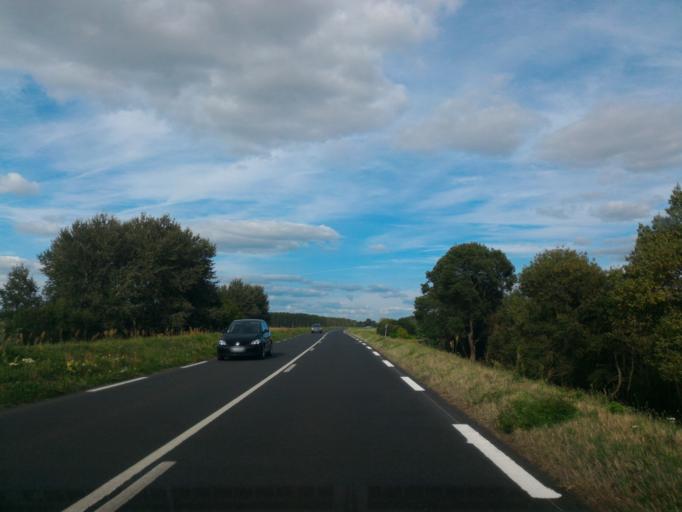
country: FR
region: Centre
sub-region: Departement du Loir-et-Cher
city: Onzain
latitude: 47.4806
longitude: 1.1627
